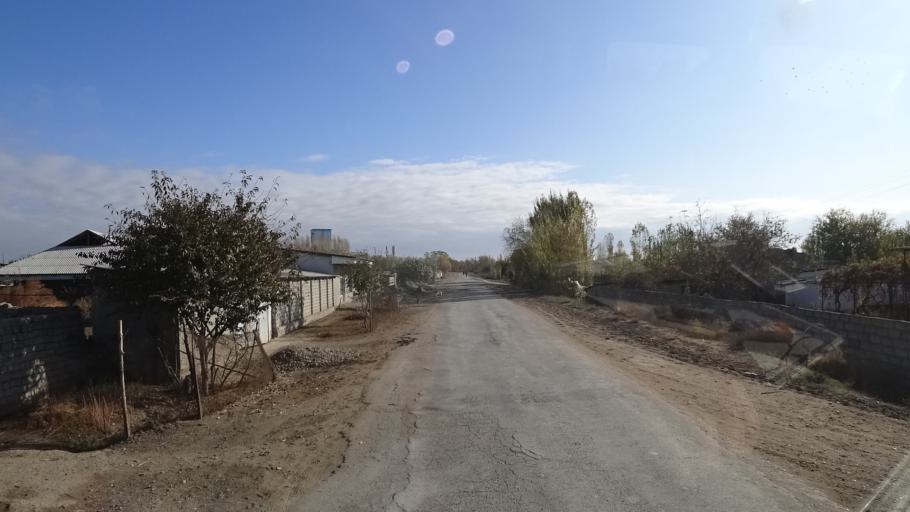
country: UZ
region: Sirdaryo
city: Sirdaryo
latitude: 40.9035
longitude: 68.6852
